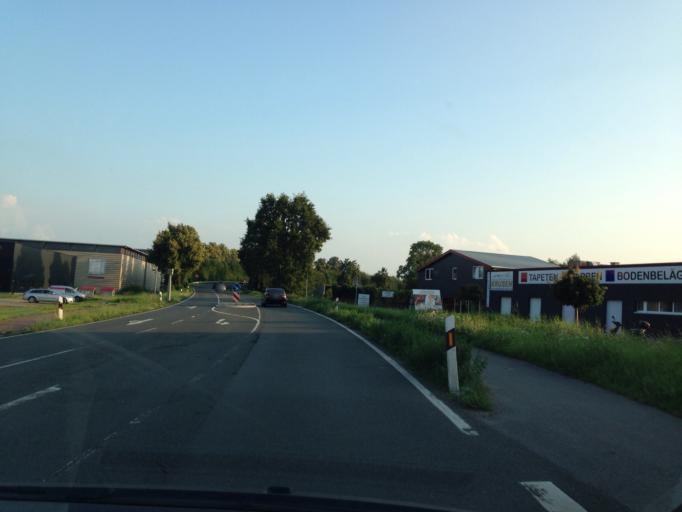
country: DE
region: North Rhine-Westphalia
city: Ludinghausen
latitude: 51.7546
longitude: 7.4302
